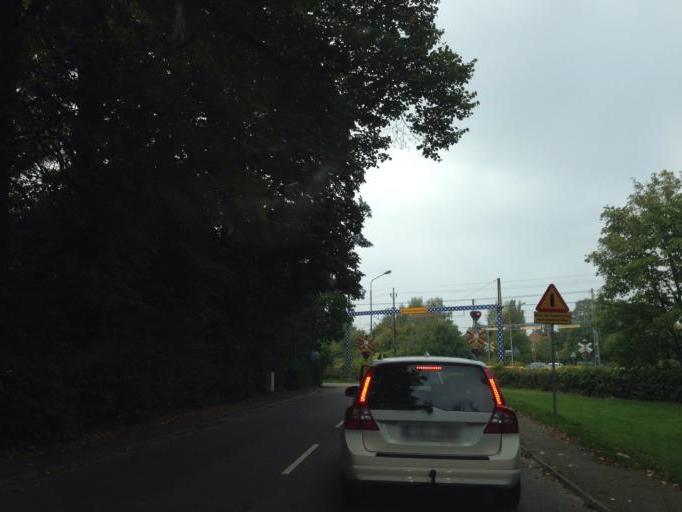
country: SE
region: Skane
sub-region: Staffanstorps Kommun
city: Hjaerup
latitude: 55.6540
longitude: 13.1039
